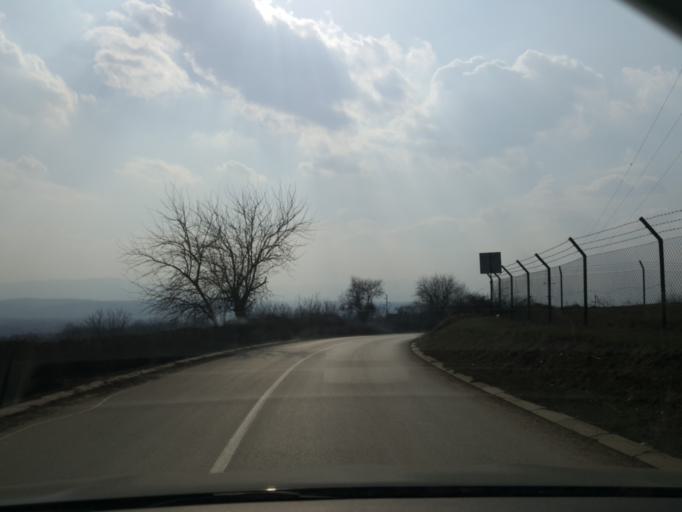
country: RS
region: Central Serbia
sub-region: Nisavski Okrug
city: Aleksinac
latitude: 43.5376
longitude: 21.7256
